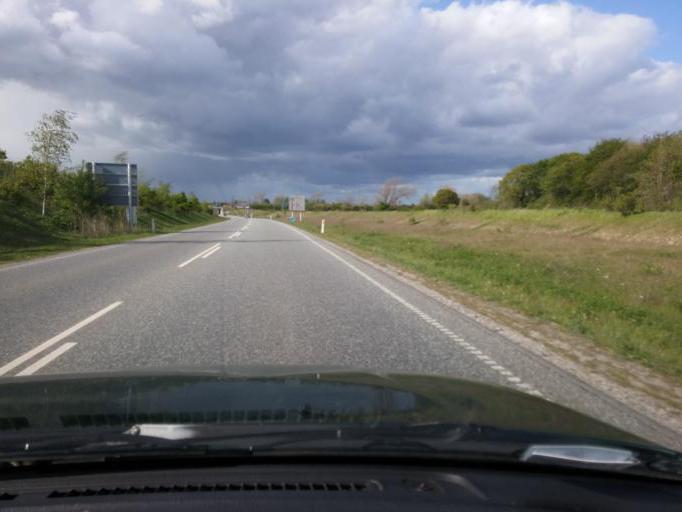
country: DK
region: South Denmark
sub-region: Odense Kommune
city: Neder Holluf
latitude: 55.3803
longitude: 10.4800
